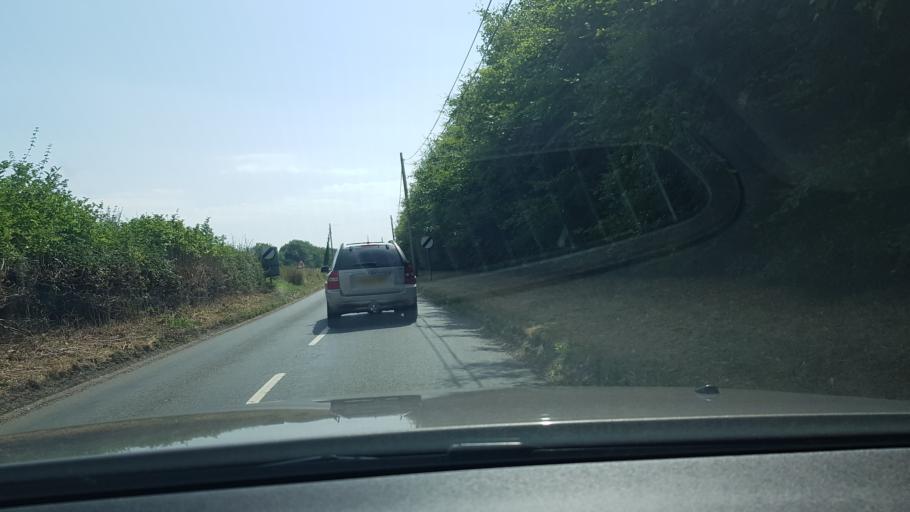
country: GB
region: England
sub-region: West Berkshire
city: Wickham
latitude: 51.4846
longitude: -1.4731
